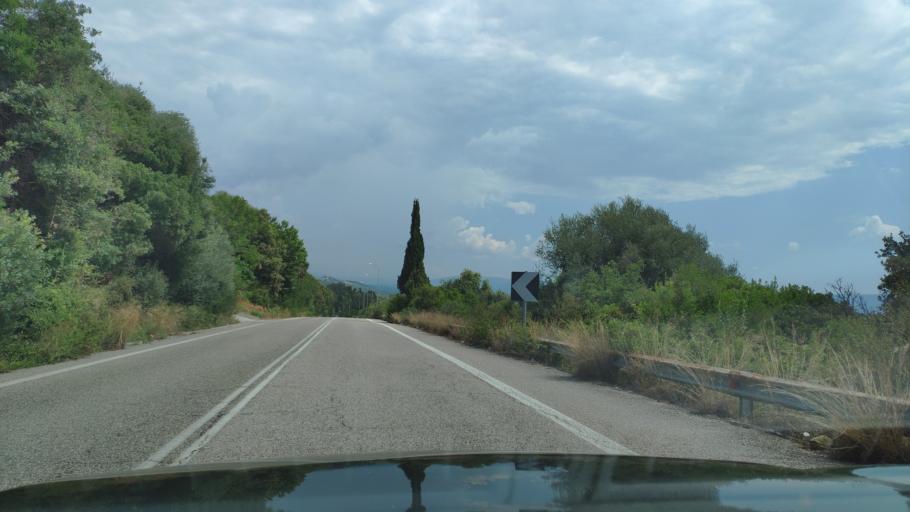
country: GR
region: West Greece
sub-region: Nomos Aitolias kai Akarnanias
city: Menidi
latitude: 38.9983
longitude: 21.1511
